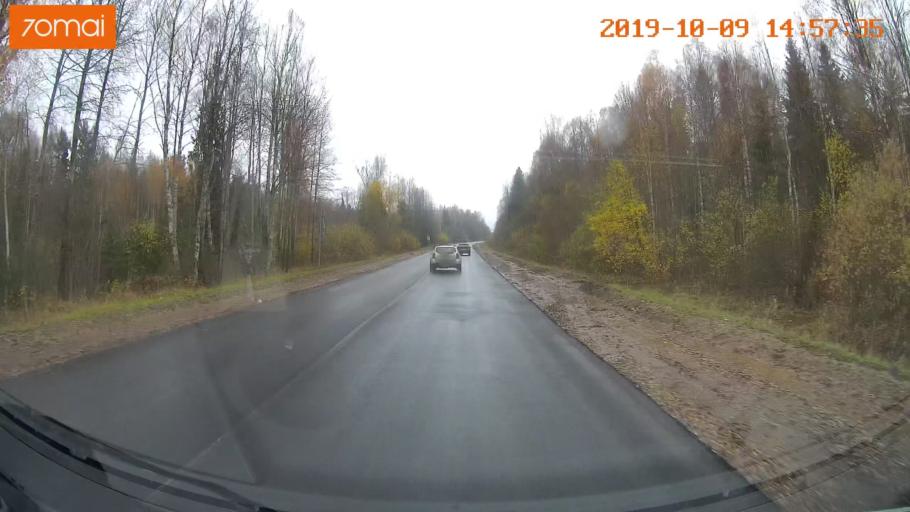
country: RU
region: Kostroma
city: Chistyye Bory
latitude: 58.3361
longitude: 41.6515
